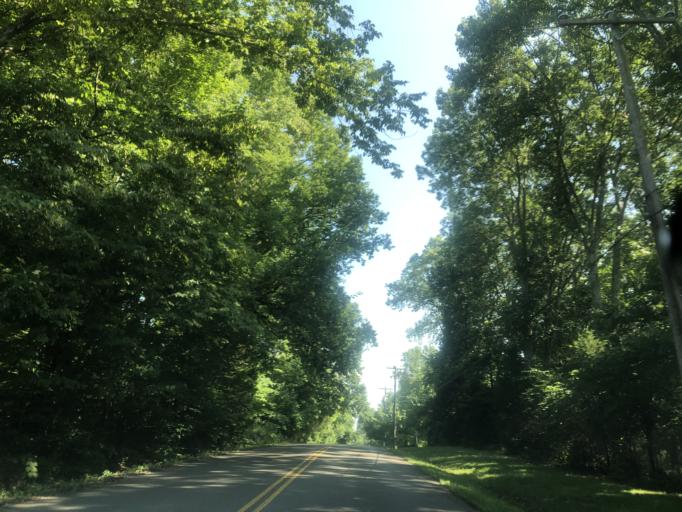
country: US
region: Tennessee
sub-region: Wilson County
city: Green Hill
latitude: 36.1437
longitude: -86.5953
